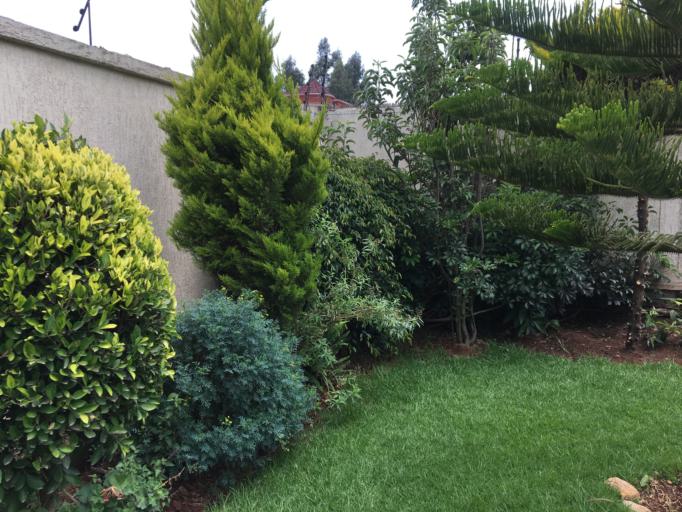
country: ET
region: Adis Abeba
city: Addis Ababa
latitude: 9.0635
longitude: 38.8896
